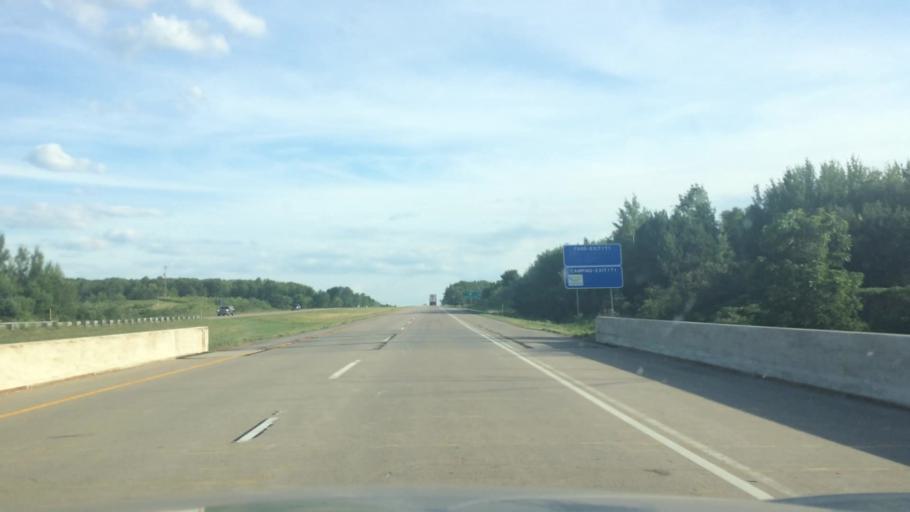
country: US
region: Wisconsin
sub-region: Marathon County
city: Mosinee
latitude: 44.6840
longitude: -89.6415
